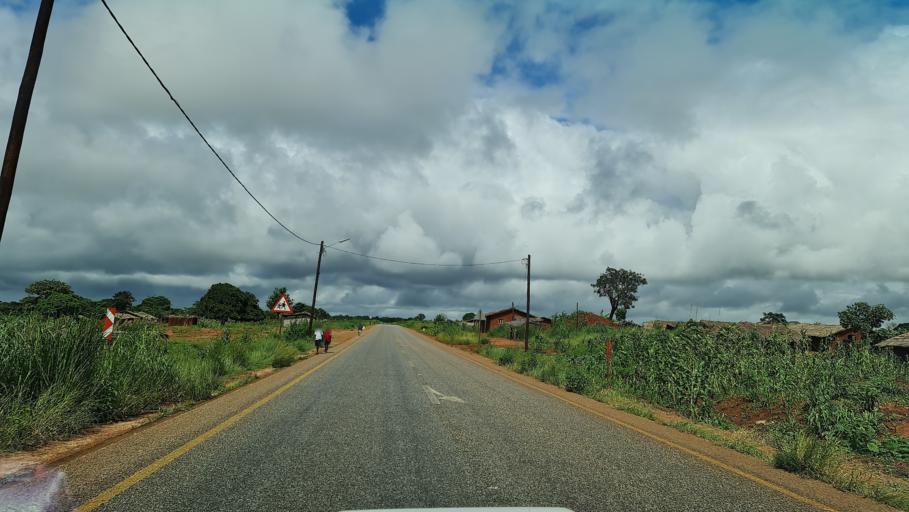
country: MZ
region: Nampula
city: Nampula
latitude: -15.0278
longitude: 38.4561
